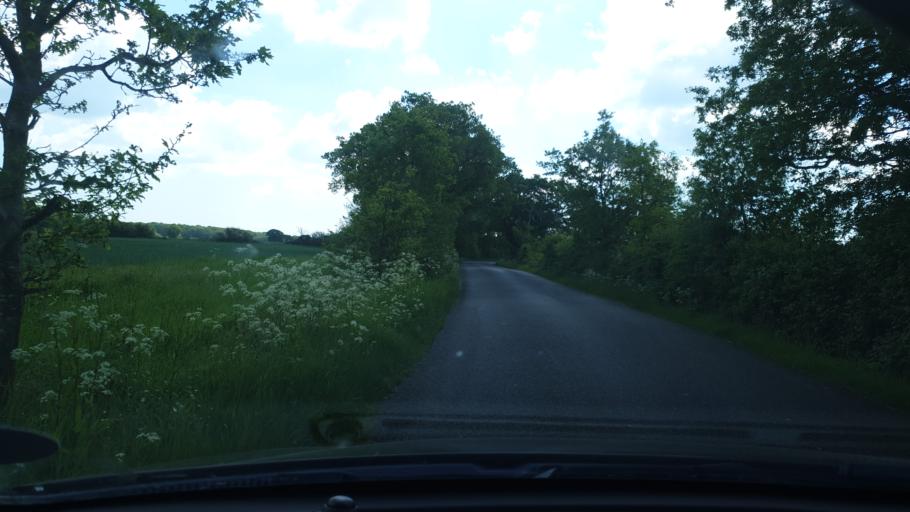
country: GB
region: England
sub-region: Essex
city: Great Bentley
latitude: 51.8473
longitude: 1.0893
